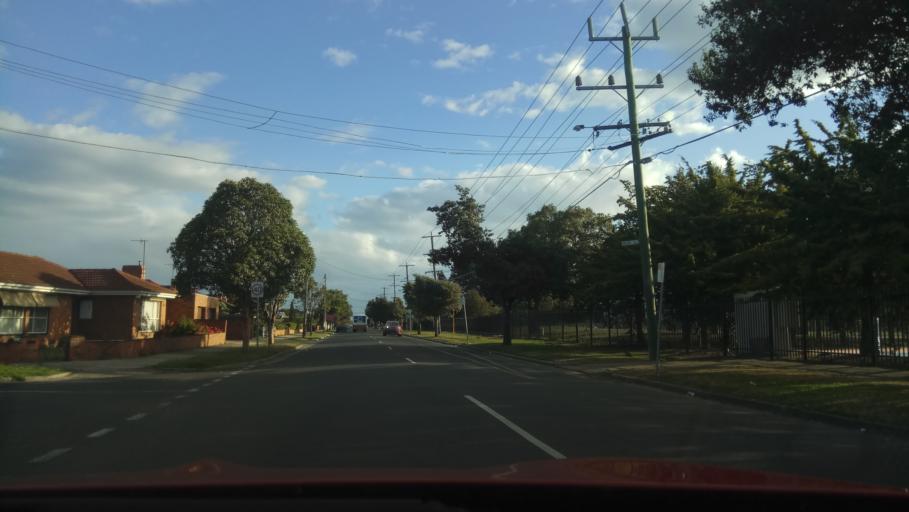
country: AU
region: Victoria
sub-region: Hobsons Bay
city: Altona North
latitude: -37.8325
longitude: 144.8430
